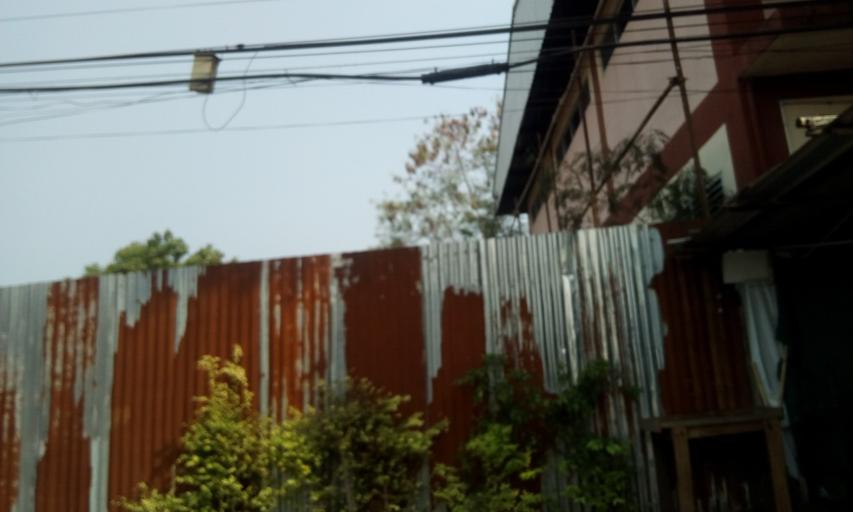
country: TH
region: Pathum Thani
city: Lam Luk Ka
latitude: 13.9367
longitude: 100.7203
